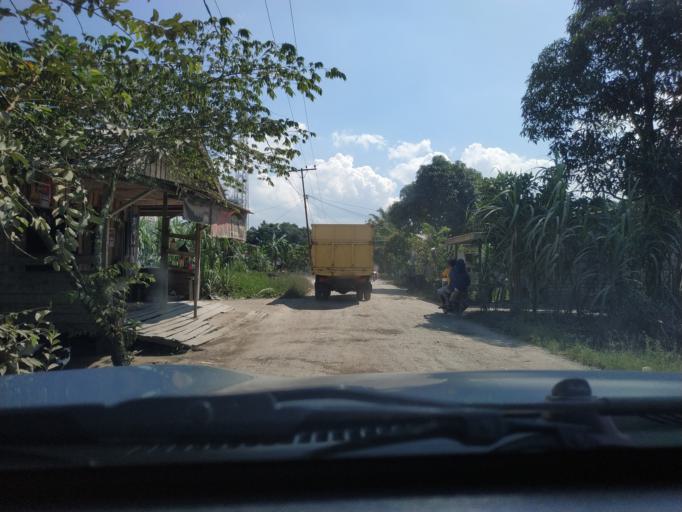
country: ID
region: North Sumatra
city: Tanjungbalai
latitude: 2.8745
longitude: 99.8604
